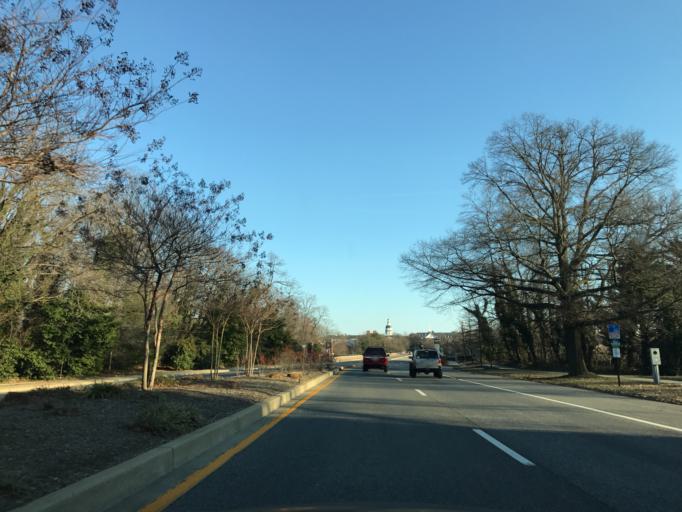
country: US
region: Maryland
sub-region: Anne Arundel County
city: Annapolis
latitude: 38.9848
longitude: -76.4993
